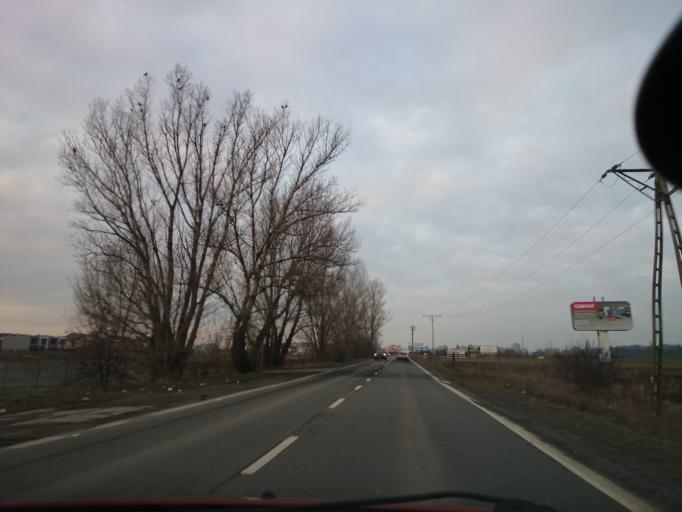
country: PL
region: Opole Voivodeship
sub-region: Powiat opolski
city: Opole
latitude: 50.6478
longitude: 17.9106
